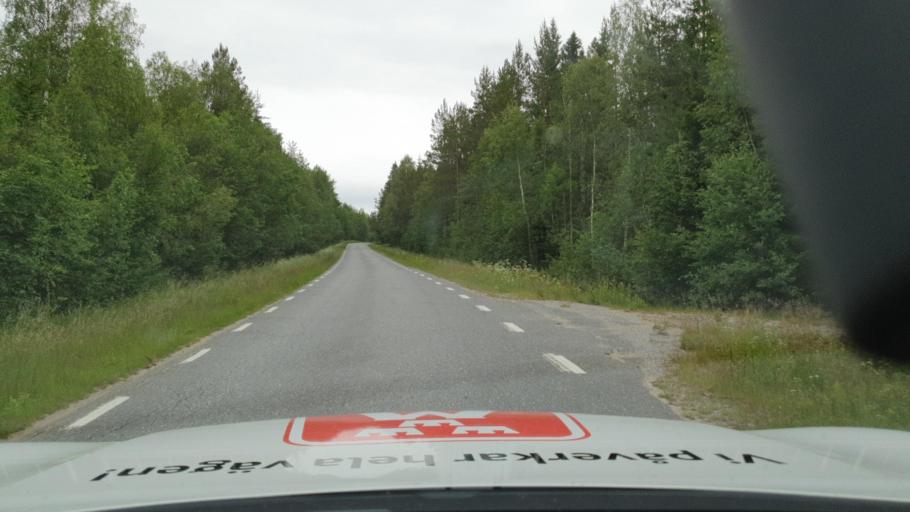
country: SE
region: Vaesterbotten
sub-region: Nordmalings Kommun
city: Nordmaling
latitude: 63.4804
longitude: 19.4562
